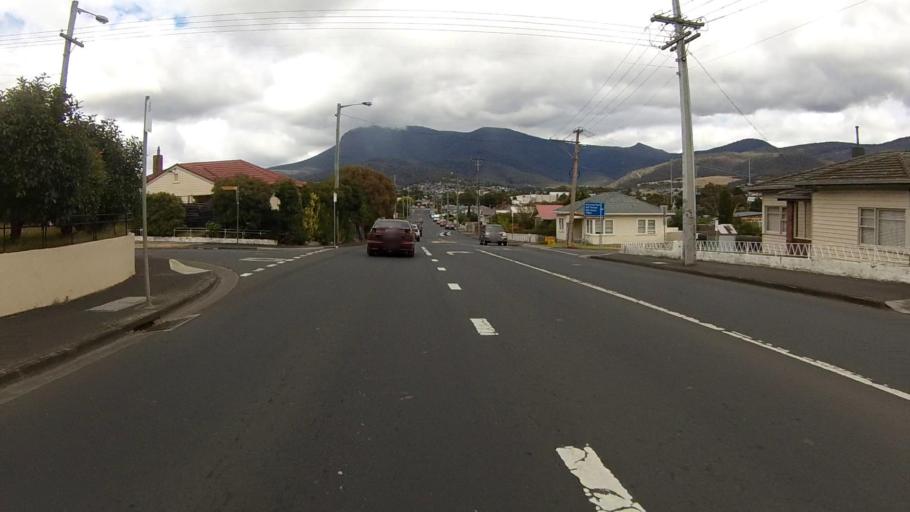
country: AU
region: Tasmania
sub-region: Glenorchy
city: Glenorchy
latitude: -42.8298
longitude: 147.2825
